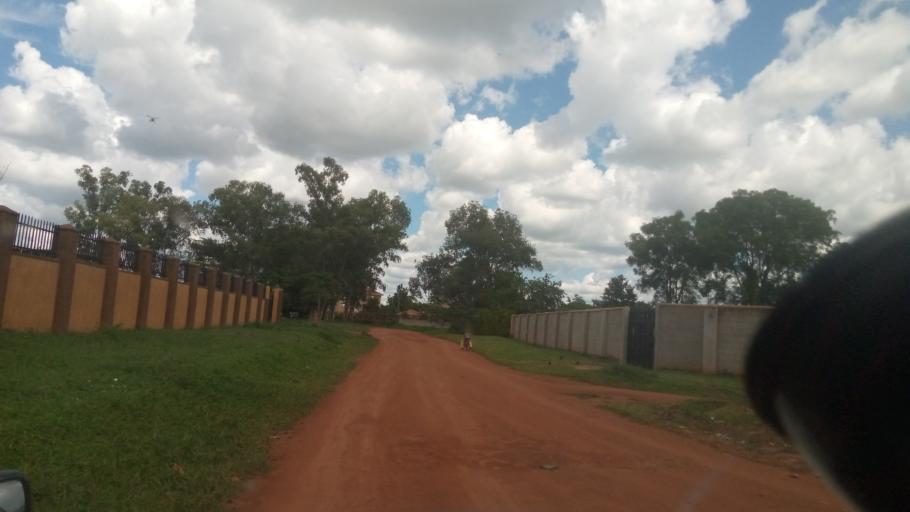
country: UG
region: Northern Region
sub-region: Lira District
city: Lira
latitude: 2.2390
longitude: 32.9055
